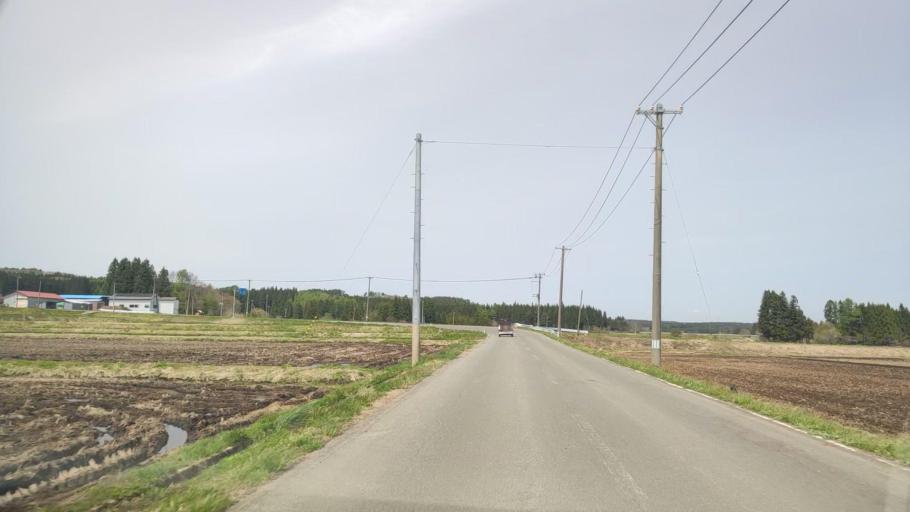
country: JP
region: Aomori
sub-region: Misawa Shi
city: Inuotose
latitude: 40.7623
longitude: 141.1199
